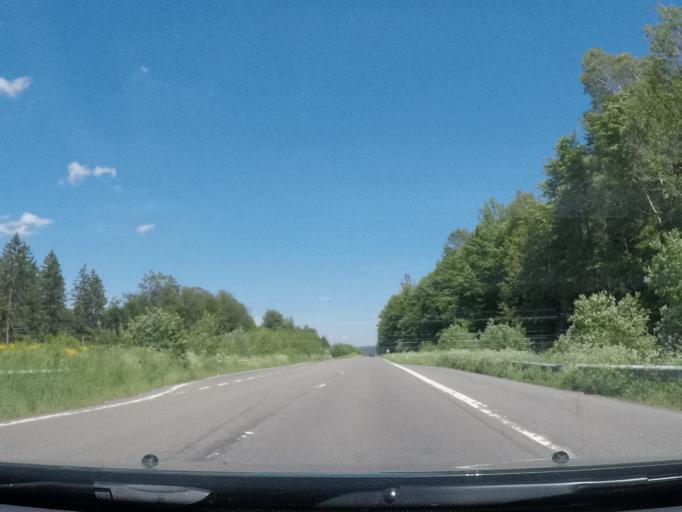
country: BE
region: Wallonia
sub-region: Province du Luxembourg
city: Saint-Hubert
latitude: 49.9500
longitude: 5.3504
